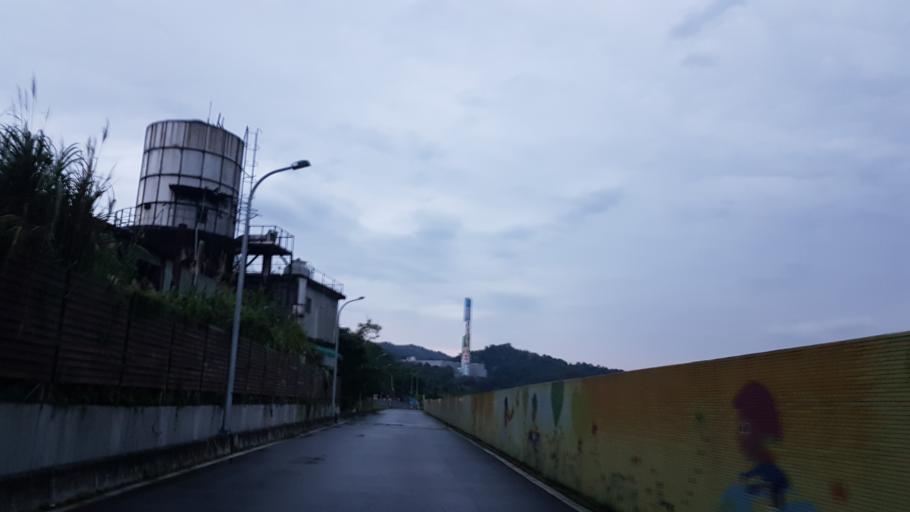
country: TW
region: Taipei
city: Taipei
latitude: 24.9996
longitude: 121.5769
